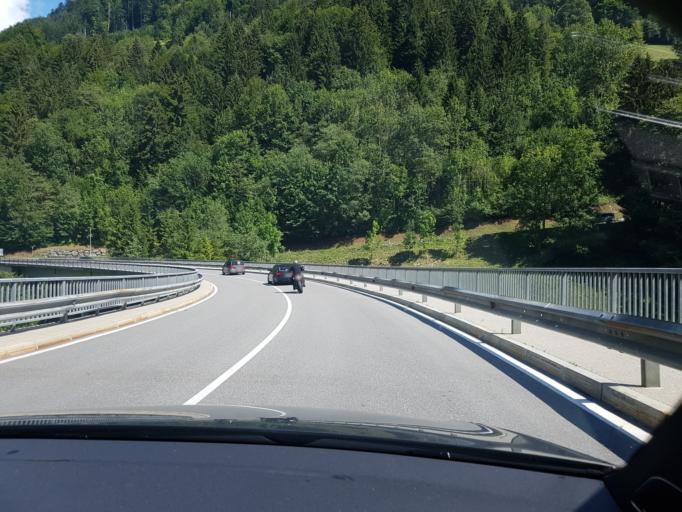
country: AT
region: Vorarlberg
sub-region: Politischer Bezirk Bludenz
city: Raggal
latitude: 47.2070
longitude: 9.8535
